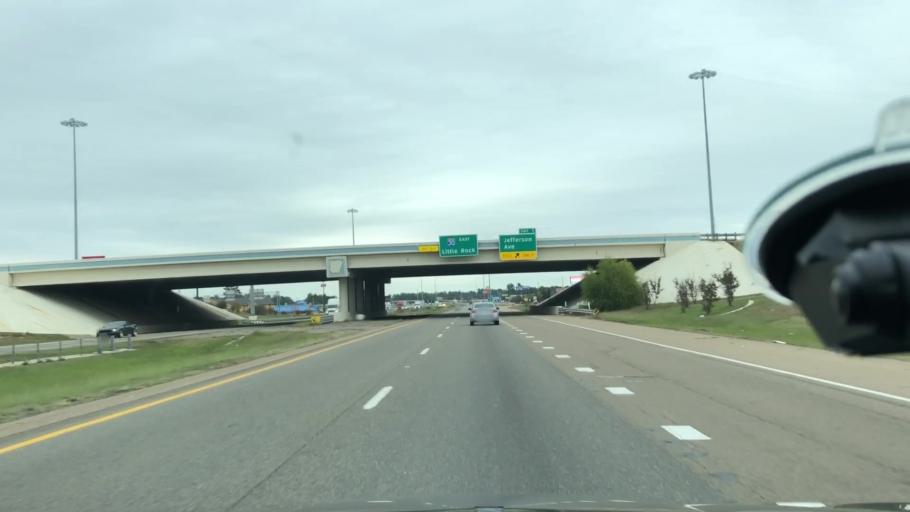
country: US
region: Arkansas
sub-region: Miller County
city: Texarkana
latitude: 33.4701
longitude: -94.0444
